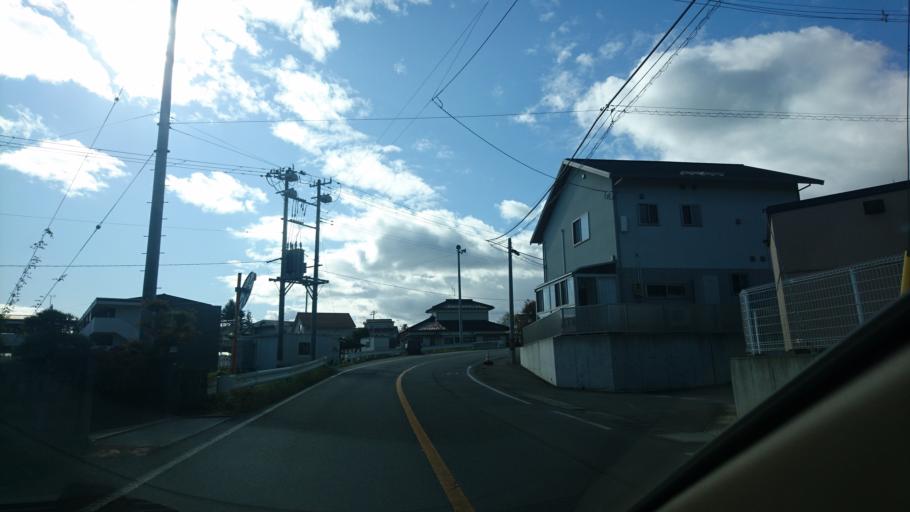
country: JP
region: Iwate
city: Ofunato
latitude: 39.0071
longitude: 141.7102
